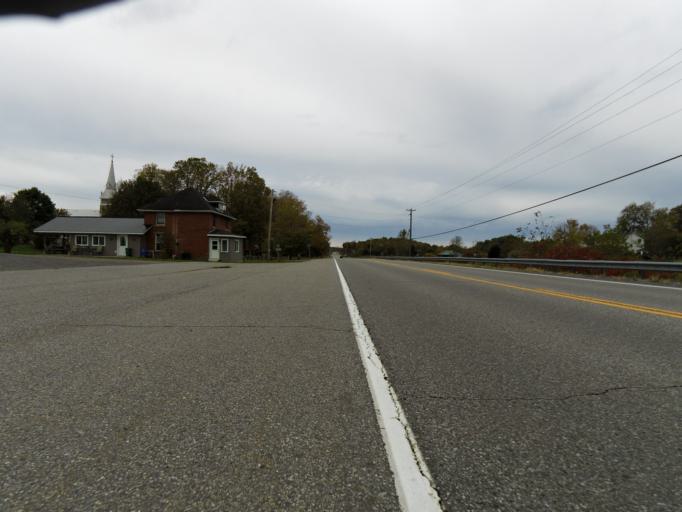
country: CA
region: Ontario
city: Gananoque
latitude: 44.4173
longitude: -76.3048
